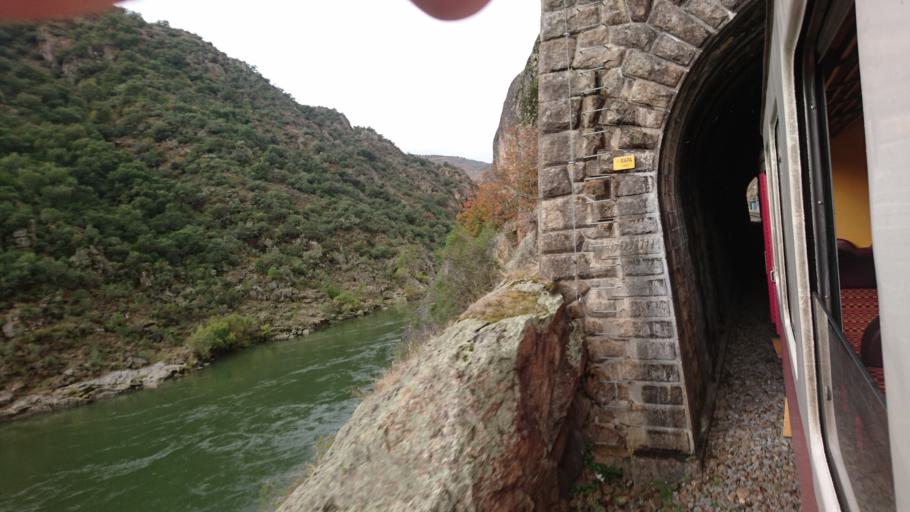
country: PT
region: Viseu
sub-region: Sao Joao da Pesqueira
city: Sao Joao da Pesqueira
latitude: 41.1978
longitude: -7.3937
